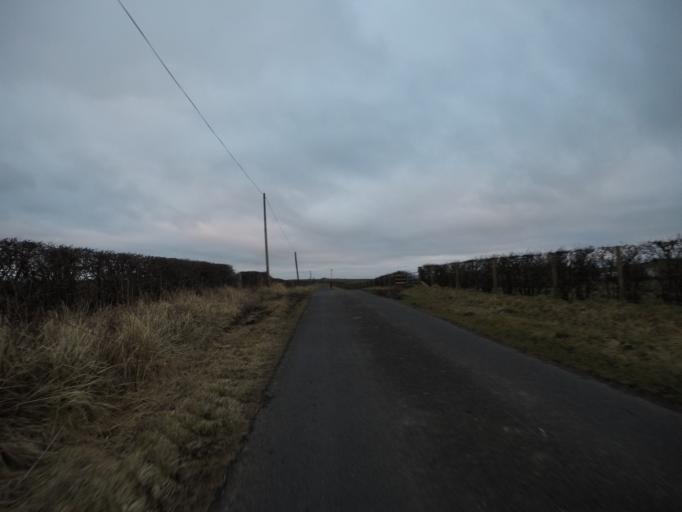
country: GB
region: Scotland
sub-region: North Ayrshire
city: Dalry
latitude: 55.6862
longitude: -4.7587
